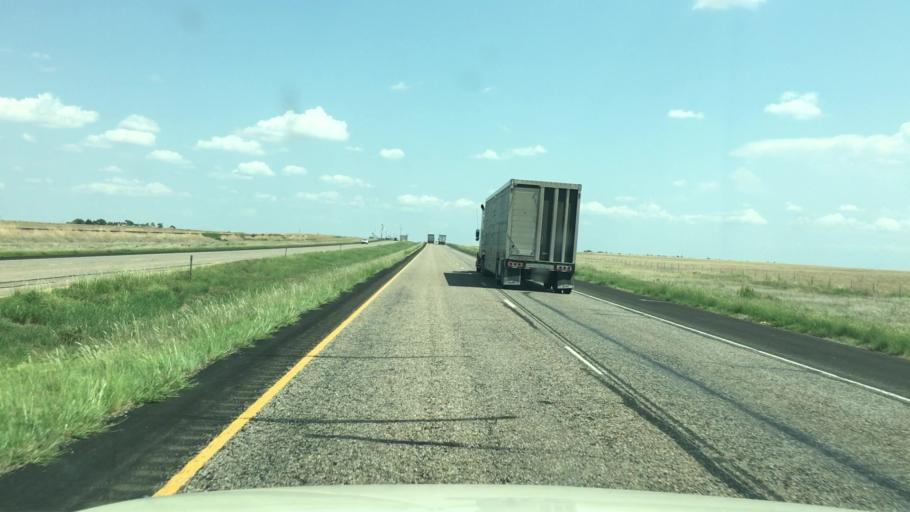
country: US
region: Texas
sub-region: Armstrong County
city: Claude
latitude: 35.1254
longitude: -101.3972
